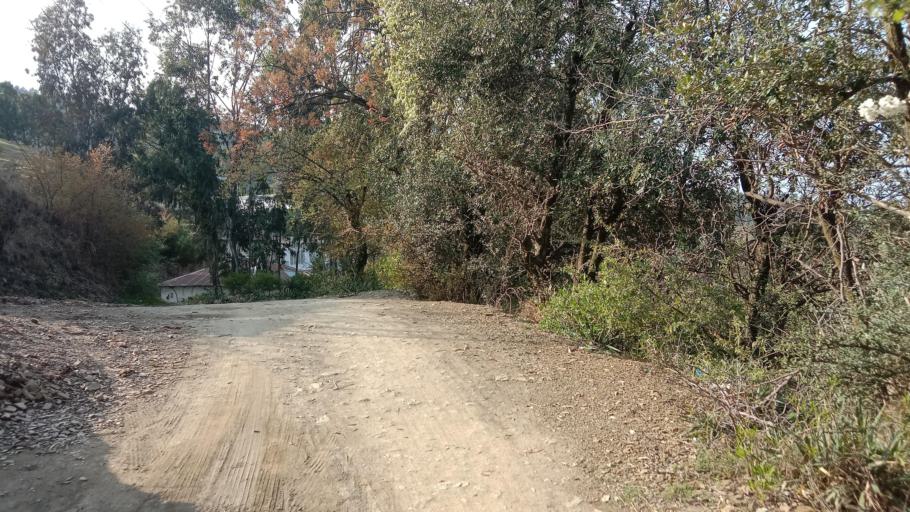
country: PK
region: Khyber Pakhtunkhwa
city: Abbottabad
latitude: 34.2042
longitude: 73.2072
